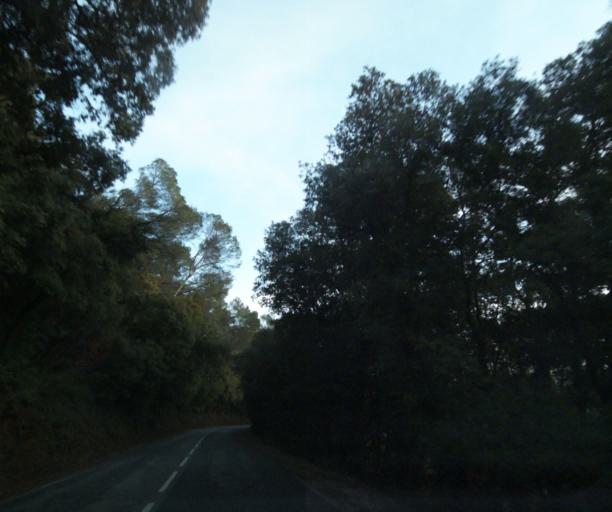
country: FR
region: Provence-Alpes-Cote d'Azur
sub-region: Departement du Var
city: Trans-en-Provence
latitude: 43.4988
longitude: 6.4983
